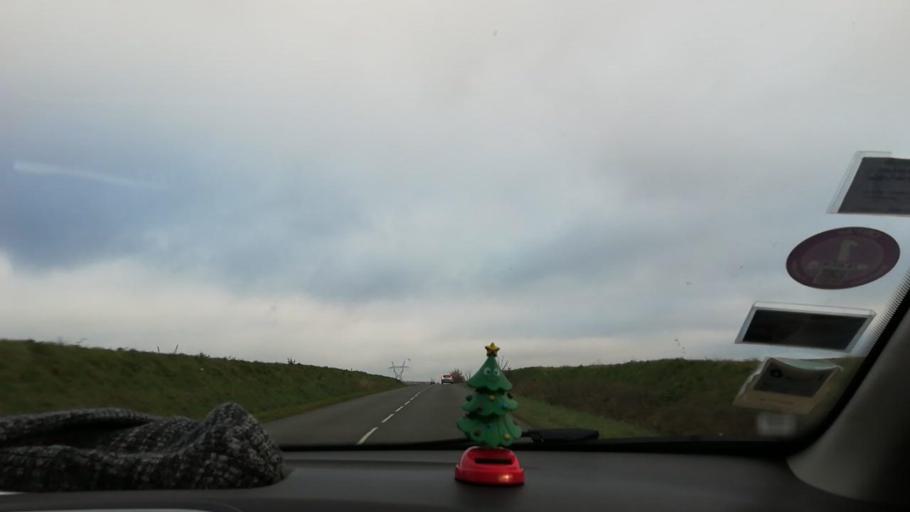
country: FR
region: Ile-de-France
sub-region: Departement de Seine-et-Marne
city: Monthyon
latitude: 48.9993
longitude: 2.8202
